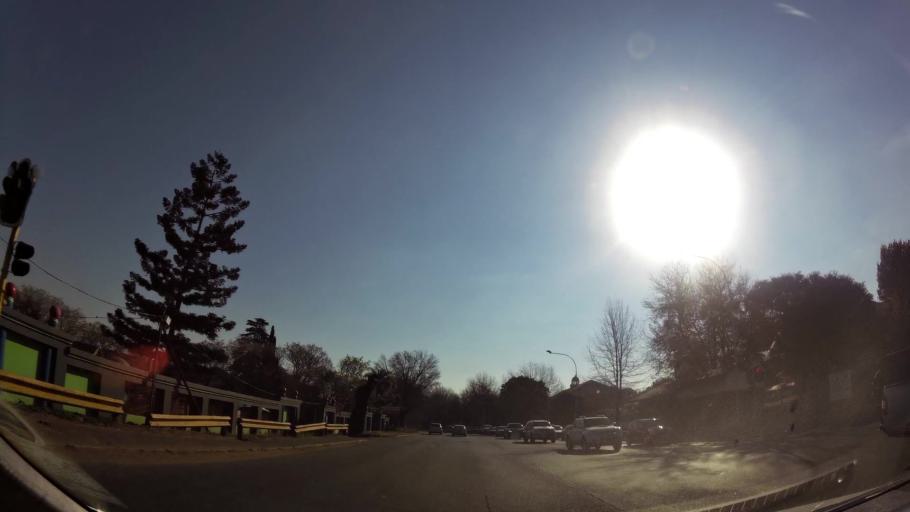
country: ZA
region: Gauteng
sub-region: Ekurhuleni Metropolitan Municipality
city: Germiston
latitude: -26.1879
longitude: 28.1359
